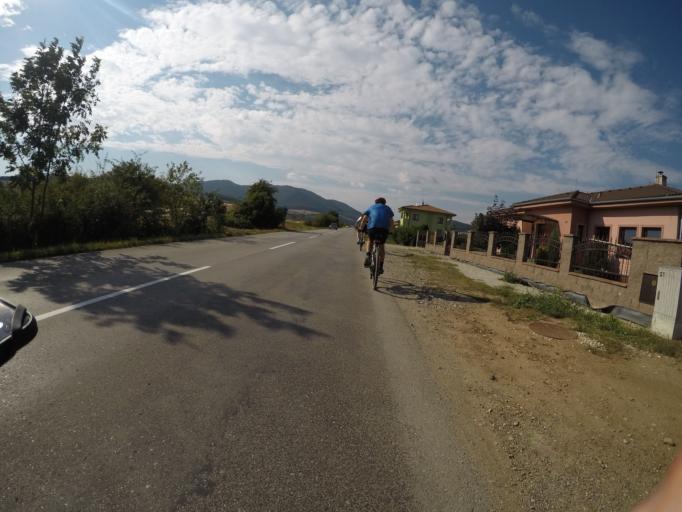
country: SK
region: Trenciansky
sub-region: Okres Trencin
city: Trencin
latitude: 48.8809
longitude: 17.9658
